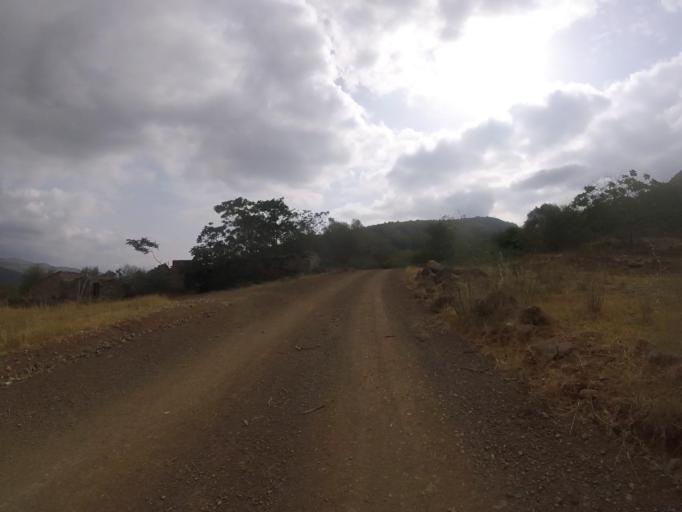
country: ES
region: Valencia
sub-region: Provincia de Castello
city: Santa Magdalena de Pulpis
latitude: 40.3495
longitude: 0.3069
